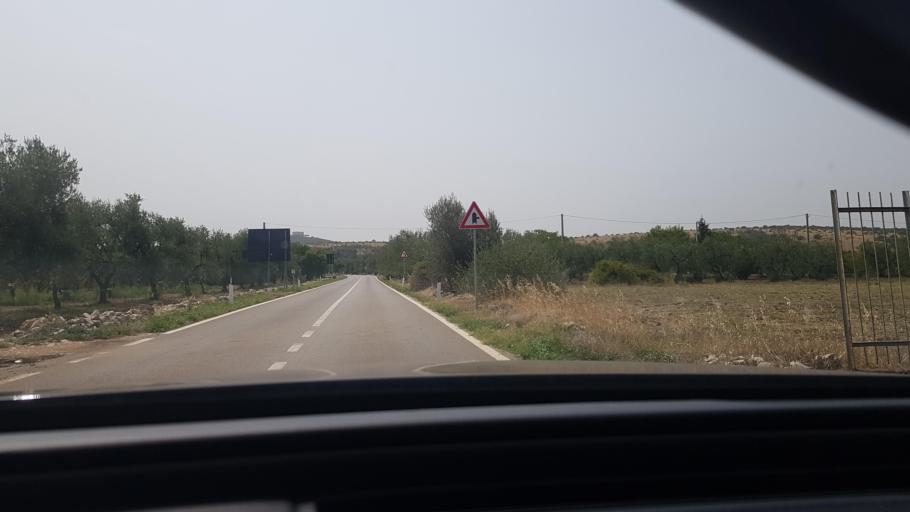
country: IT
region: Apulia
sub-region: Provincia di Barletta - Andria - Trani
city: Andria
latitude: 41.1152
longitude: 16.2820
